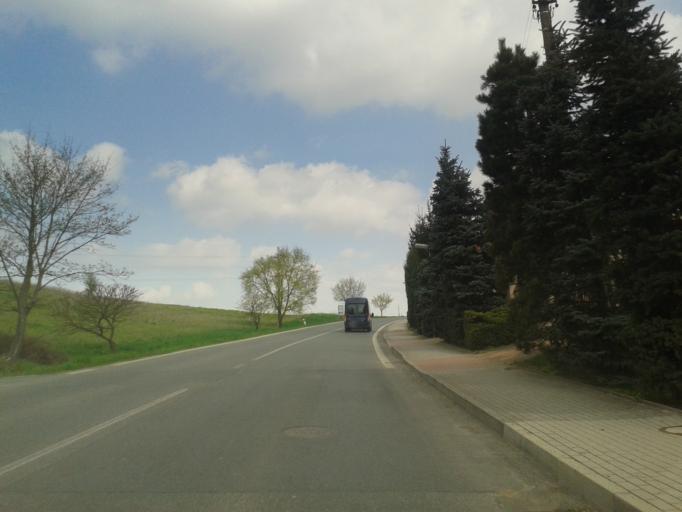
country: CZ
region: Central Bohemia
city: Zdice
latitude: 49.9188
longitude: 13.9849
